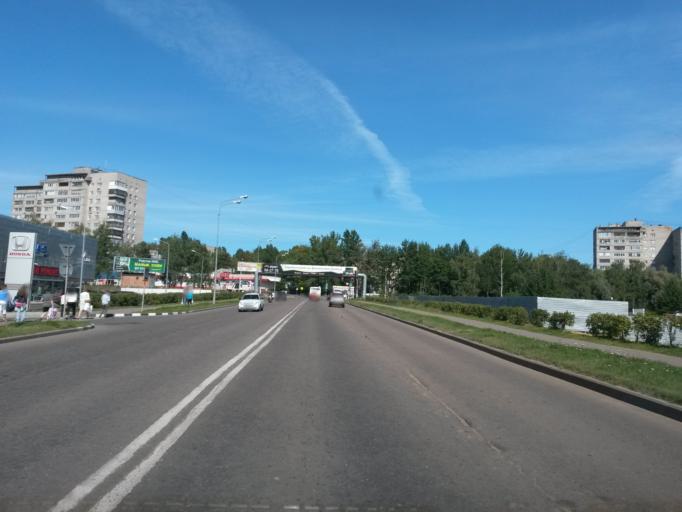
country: RU
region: Jaroslavl
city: Yaroslavl
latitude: 57.5725
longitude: 39.8484
